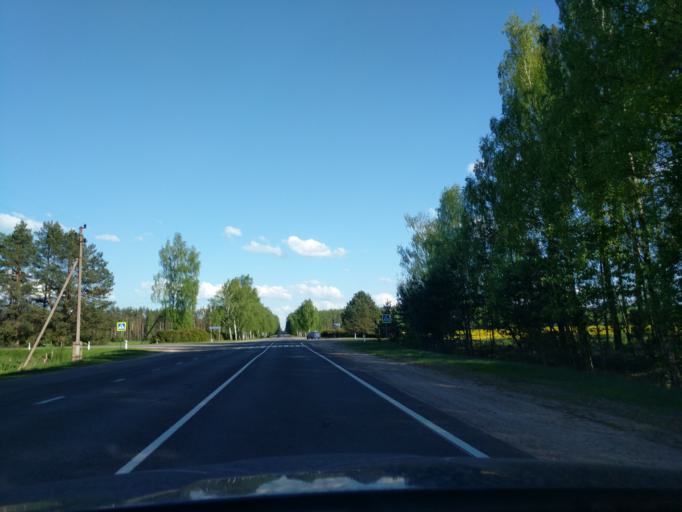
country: BY
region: Minsk
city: Myadzyel
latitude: 54.8156
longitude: 26.9694
